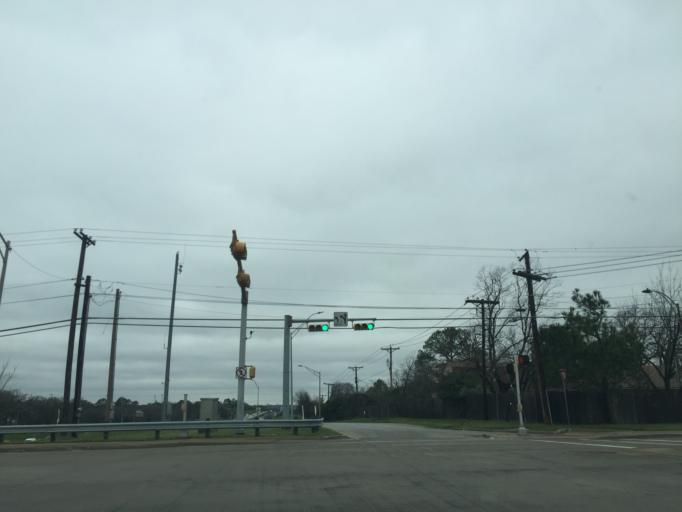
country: US
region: Texas
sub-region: Tarrant County
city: Arlington
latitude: 32.7603
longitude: -97.1314
